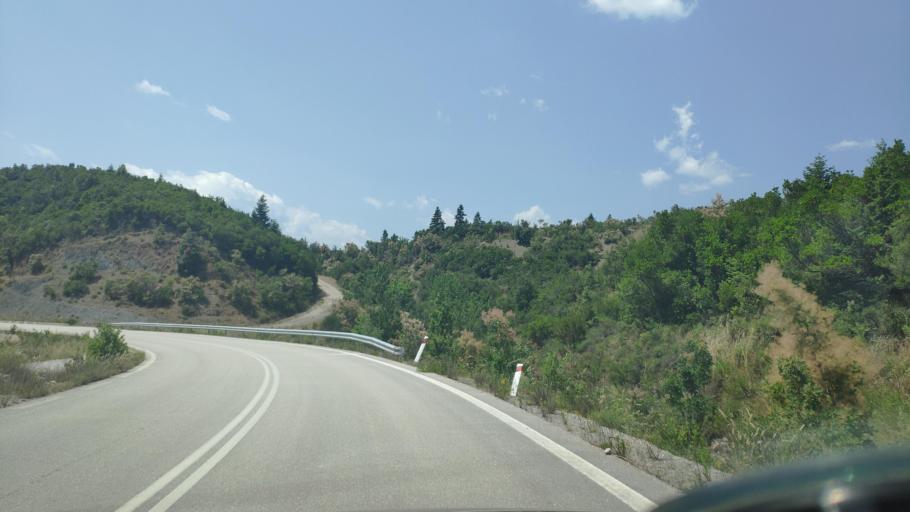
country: GR
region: Epirus
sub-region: Nomos Artas
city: Ano Kalentini
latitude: 39.2868
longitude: 21.3159
